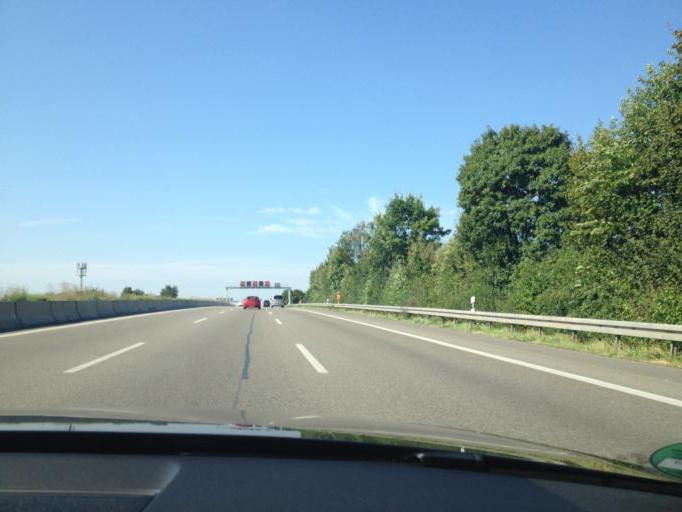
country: DE
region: Baden-Wuerttemberg
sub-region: Regierungsbezirk Stuttgart
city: Korntal
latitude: 48.8386
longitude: 9.1011
